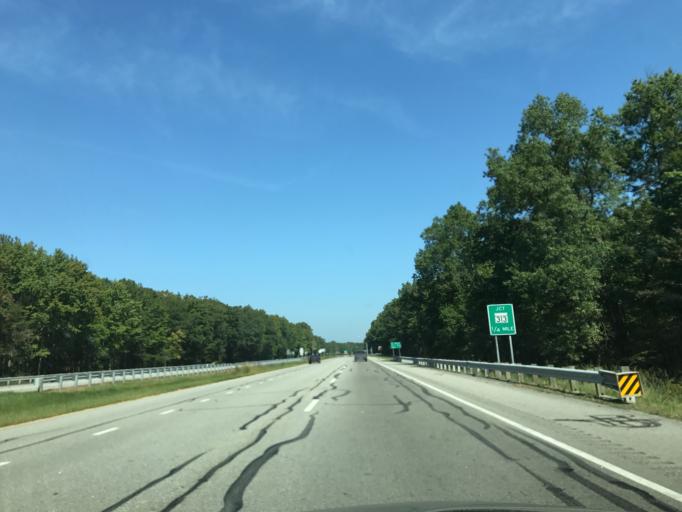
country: US
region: Delaware
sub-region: New Castle County
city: Townsend
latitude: 39.3156
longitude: -75.8476
